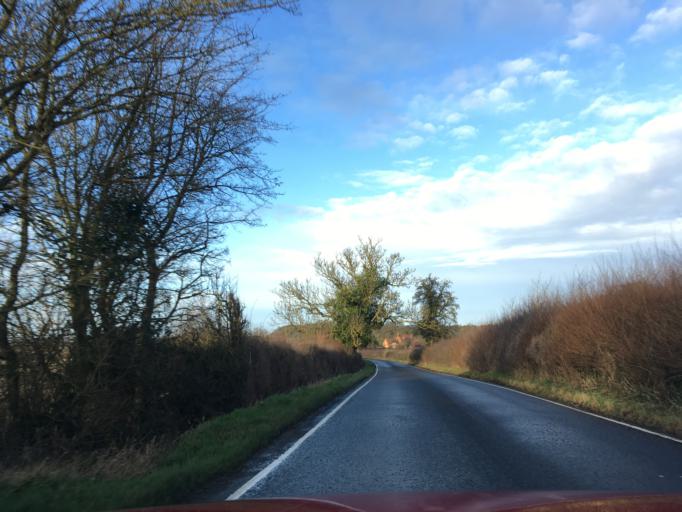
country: GB
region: England
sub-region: Warwickshire
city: Henley in Arden
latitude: 52.2218
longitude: -1.7862
